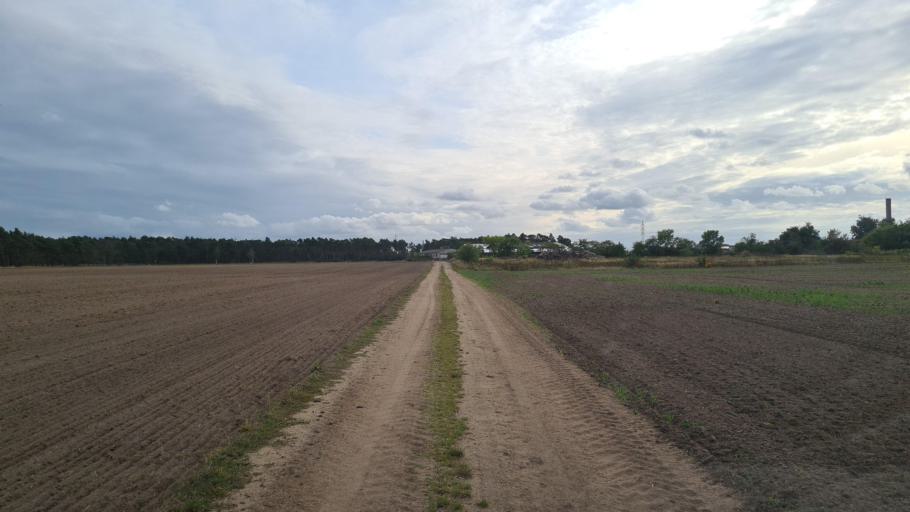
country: DE
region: Brandenburg
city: Bad Liebenwerda
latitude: 51.4758
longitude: 13.3976
